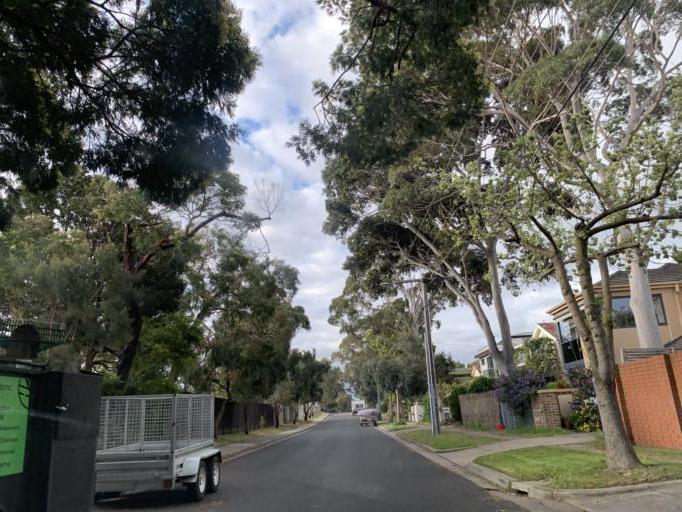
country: AU
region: Victoria
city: Beaumaris
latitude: -37.9777
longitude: 145.0386
